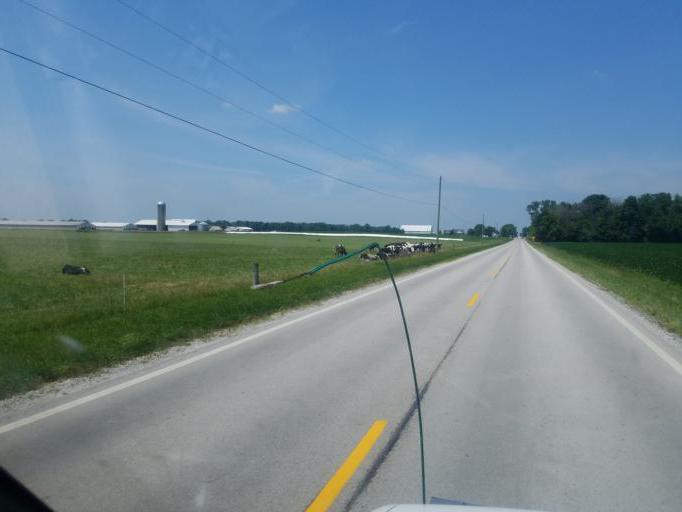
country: US
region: Ohio
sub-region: Auglaize County
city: Minster
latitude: 40.4032
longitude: -84.4339
